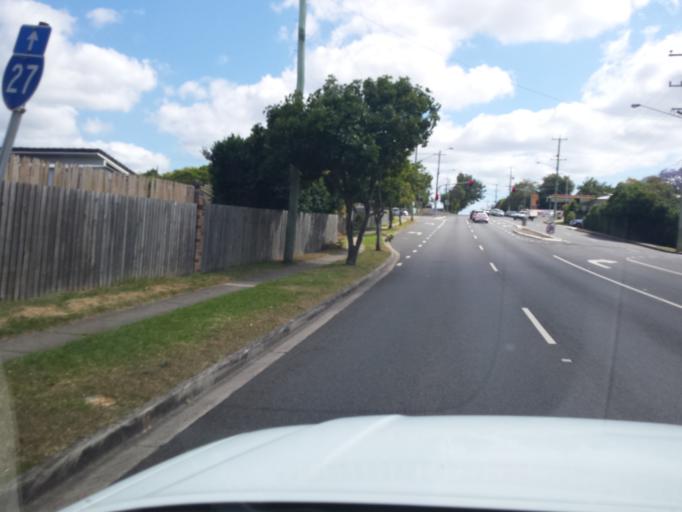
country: AU
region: Queensland
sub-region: Brisbane
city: Zillmere
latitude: -27.3680
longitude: 153.0365
